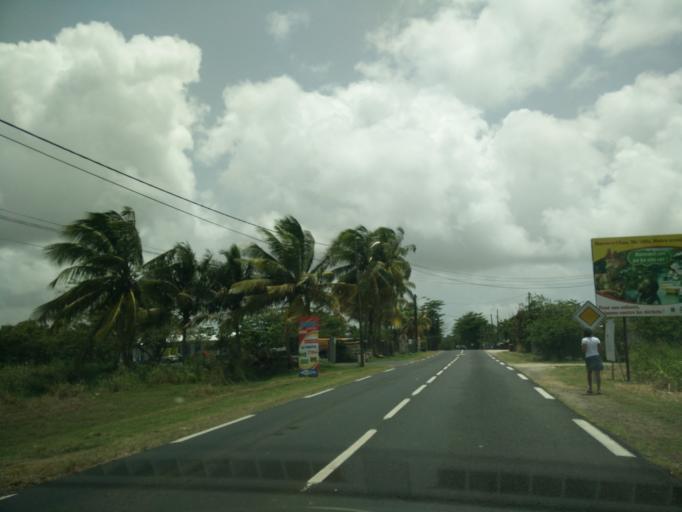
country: GP
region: Guadeloupe
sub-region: Guadeloupe
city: Petit-Canal
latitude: 16.3447
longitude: -61.4546
